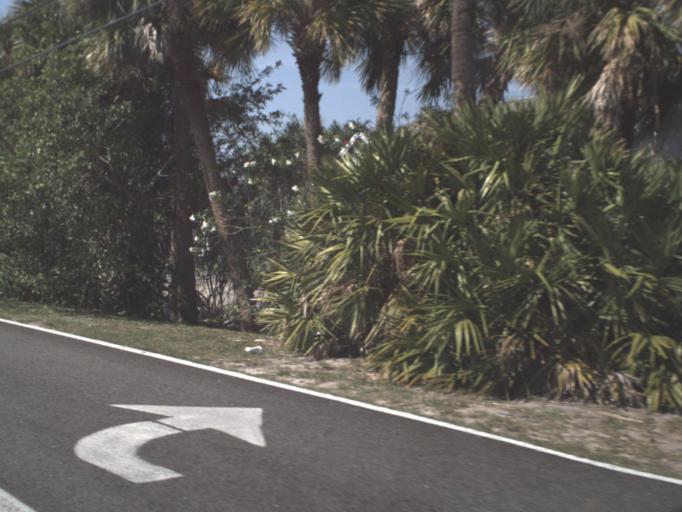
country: US
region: Florida
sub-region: Brevard County
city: Port Saint John
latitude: 28.4841
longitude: -80.7719
